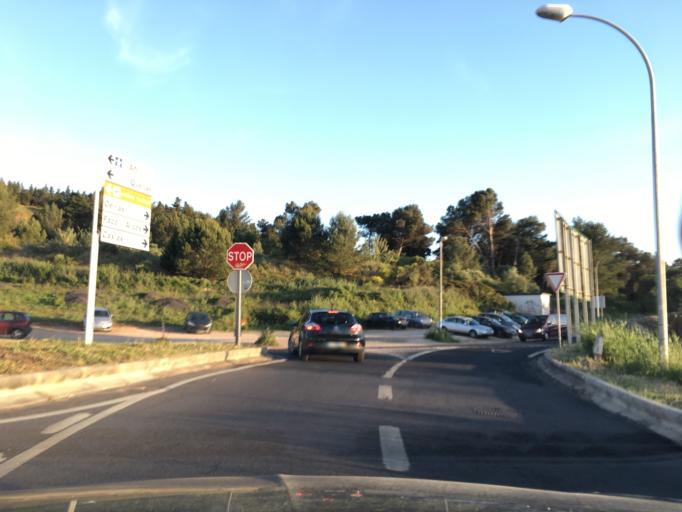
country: PT
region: Lisbon
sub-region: Oeiras
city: Quejas
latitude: 38.7080
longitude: -9.2702
